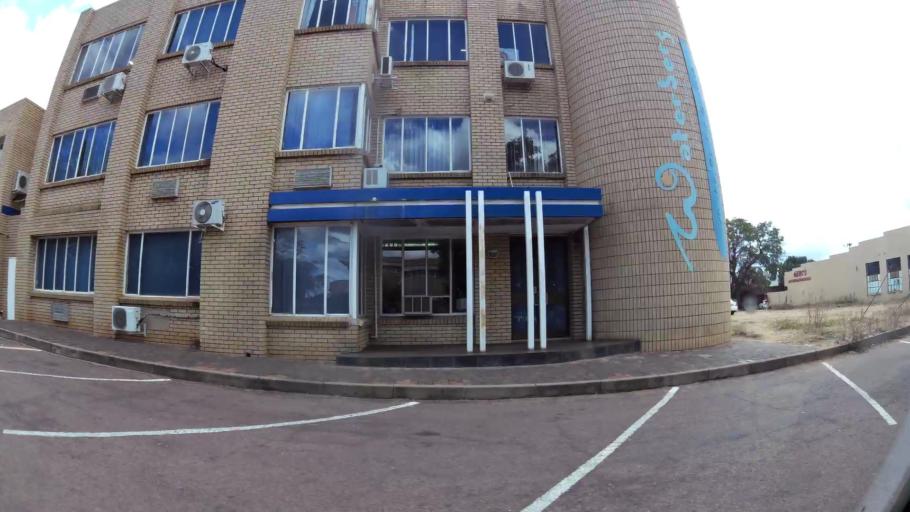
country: ZA
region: Limpopo
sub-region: Waterberg District Municipality
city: Modimolle
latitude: -24.7028
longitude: 28.4065
